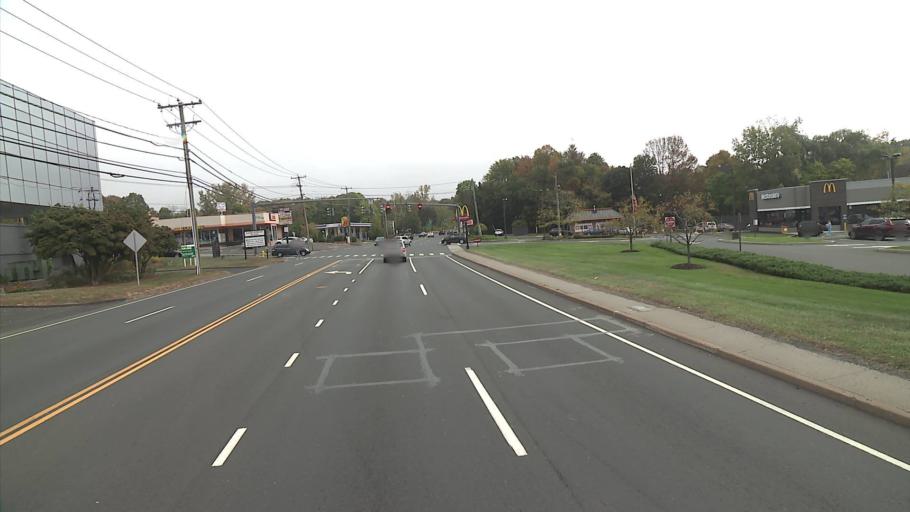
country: US
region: Connecticut
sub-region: Fairfield County
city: Danbury
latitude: 41.3868
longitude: -73.4785
